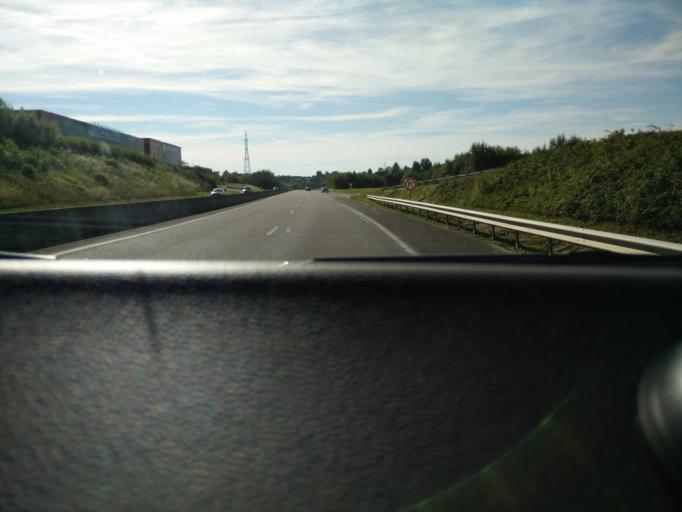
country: FR
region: Nord-Pas-de-Calais
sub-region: Departement du Nord
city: Hautmont
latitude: 50.2594
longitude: 3.9366
